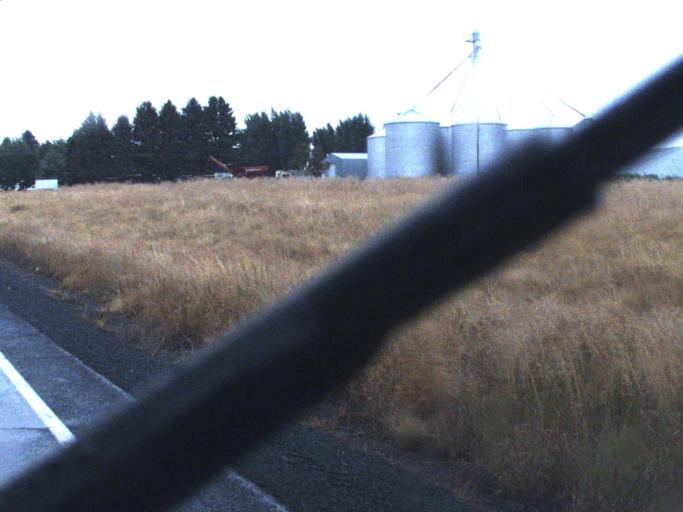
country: US
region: Washington
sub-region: Lincoln County
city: Davenport
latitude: 47.4783
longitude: -118.2232
